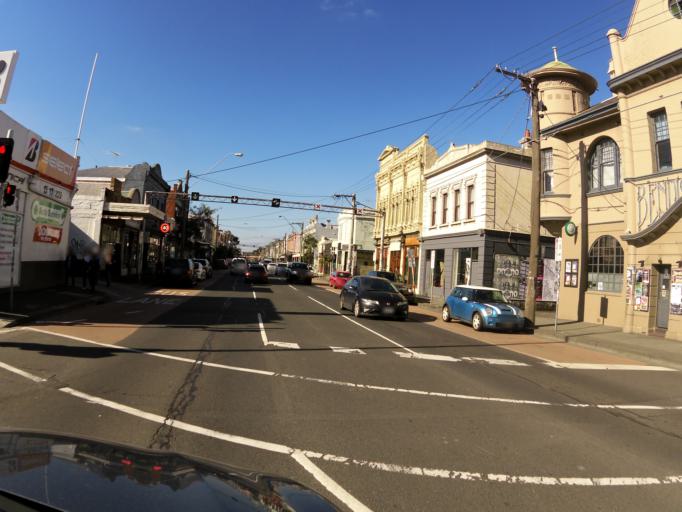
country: AU
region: Victoria
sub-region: Yarra
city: Collingwood
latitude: -37.7994
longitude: 144.9890
